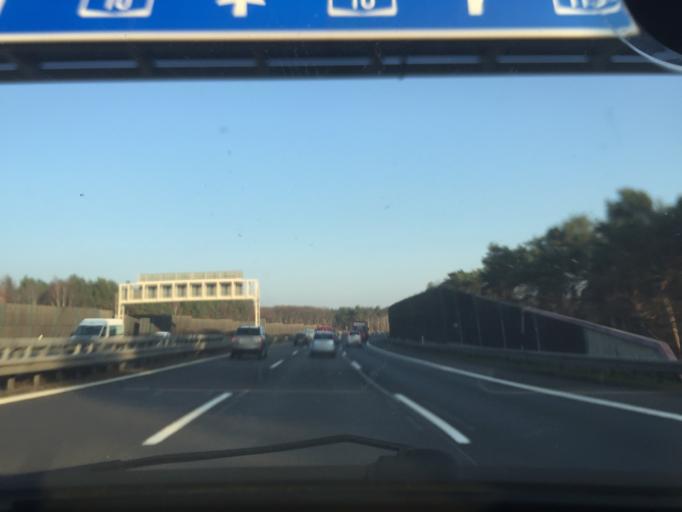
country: DE
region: Brandenburg
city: Michendorf
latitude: 52.2999
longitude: 13.0423
